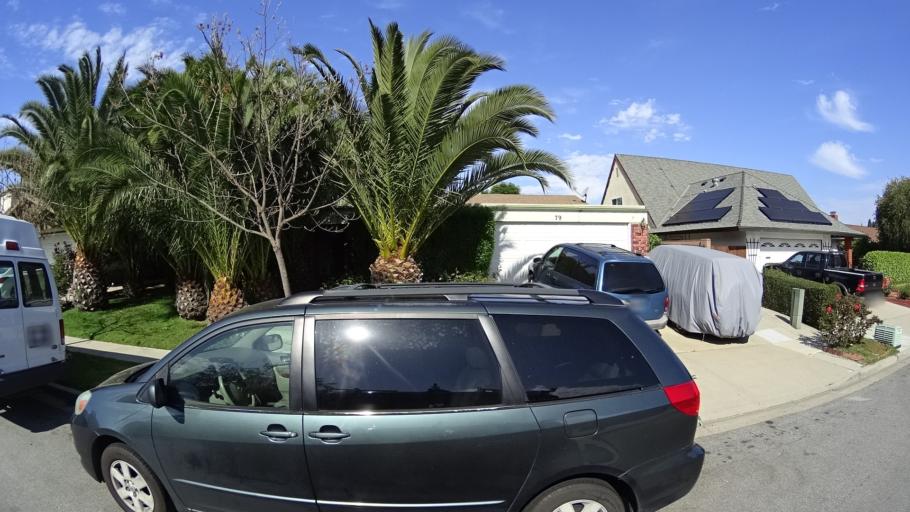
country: US
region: California
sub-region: Ventura County
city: Casa Conejo
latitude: 34.1796
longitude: -118.9238
